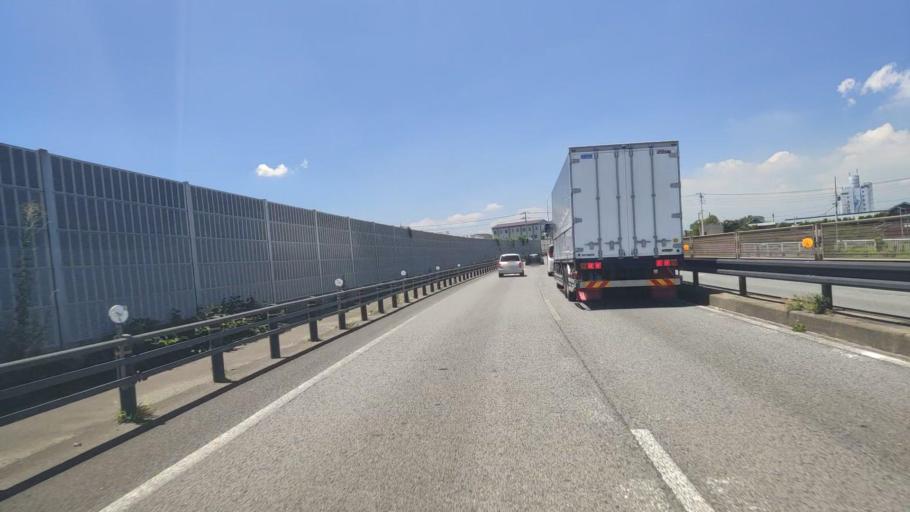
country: JP
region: Aichi
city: Kanie
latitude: 35.0682
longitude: 136.7539
